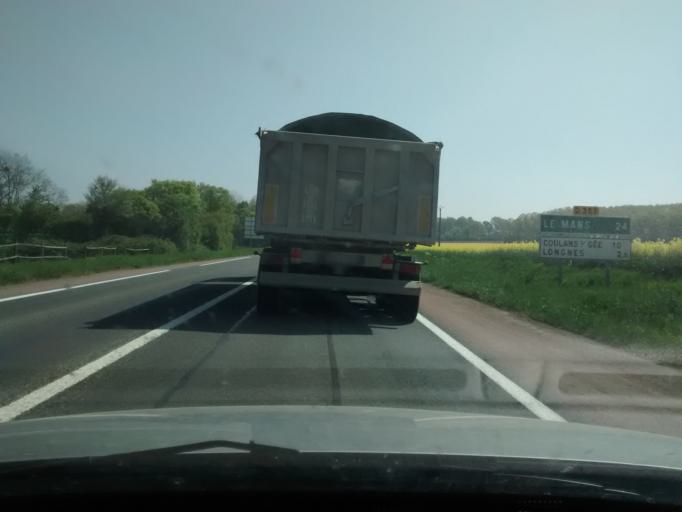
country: FR
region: Pays de la Loire
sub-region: Departement de la Sarthe
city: Loue
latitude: 48.0207
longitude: -0.1028
